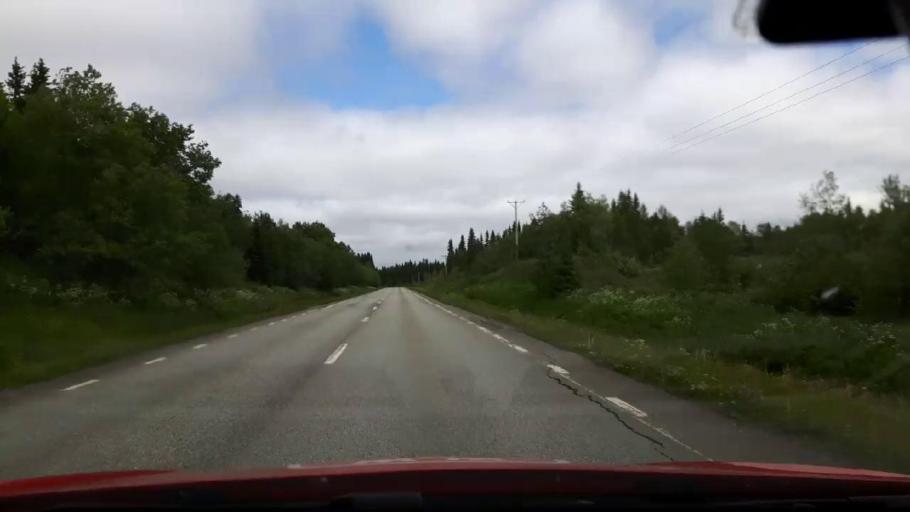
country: SE
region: Jaemtland
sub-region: Krokoms Kommun
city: Krokom
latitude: 63.5229
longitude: 14.5441
